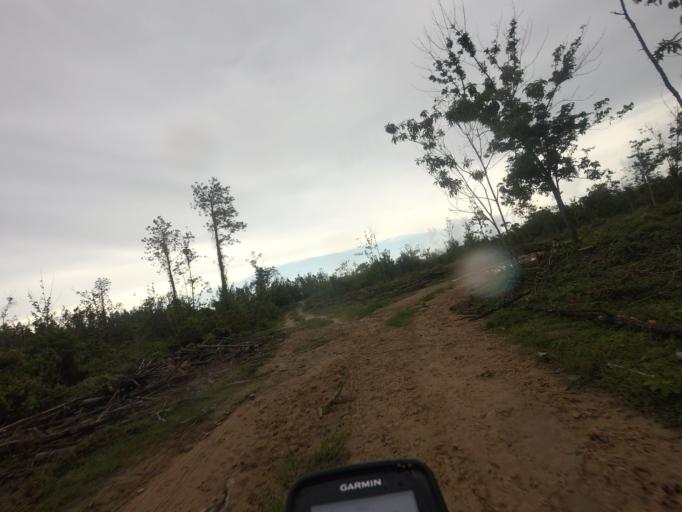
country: CU
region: Pinar del Rio
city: Vinales
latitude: 22.6033
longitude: -83.6485
